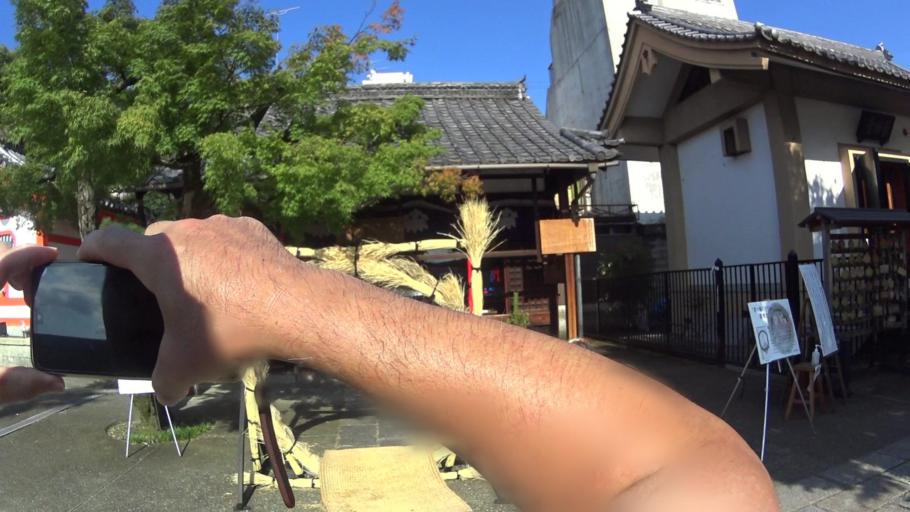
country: RU
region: Rostov
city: Remontnoye
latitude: 46.5008
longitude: 43.7632
